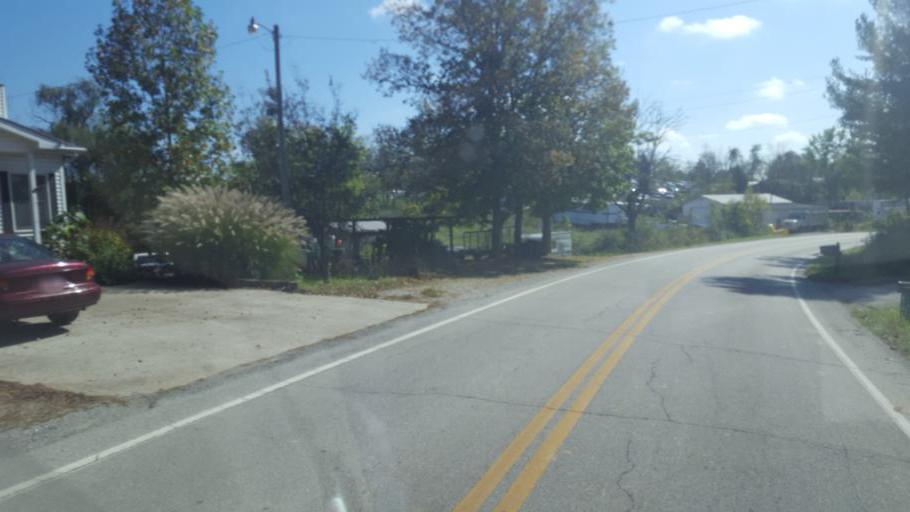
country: US
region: Kentucky
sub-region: Mason County
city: Maysville
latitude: 38.5782
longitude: -83.6471
